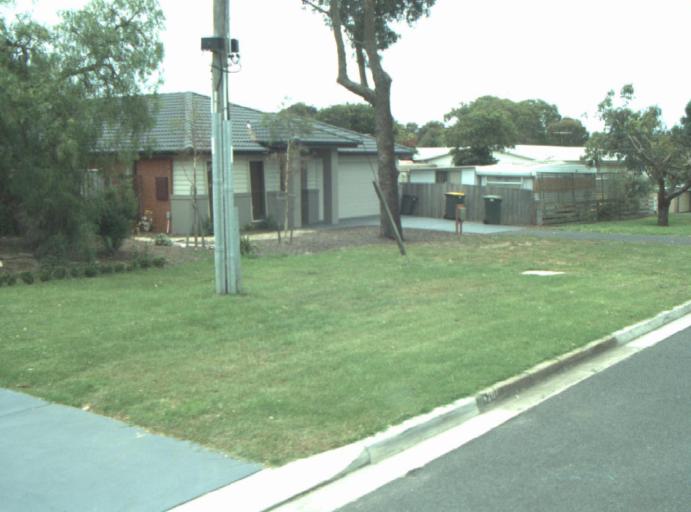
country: AU
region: Victoria
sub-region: Greater Geelong
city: Clifton Springs
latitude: -38.1168
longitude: 144.6675
